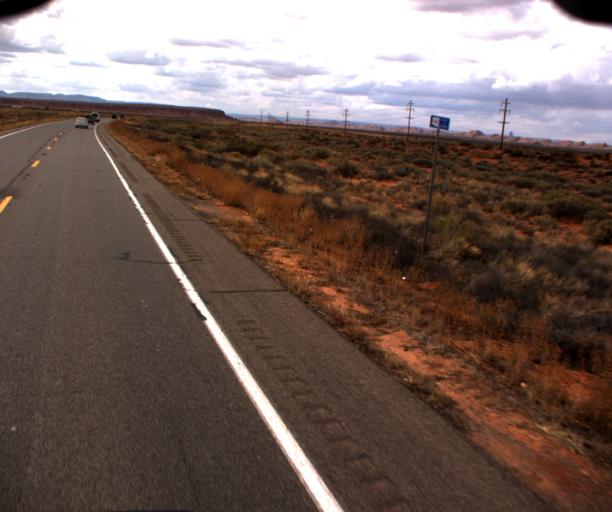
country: US
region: Arizona
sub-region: Navajo County
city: Kayenta
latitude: 36.7883
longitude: -109.9539
